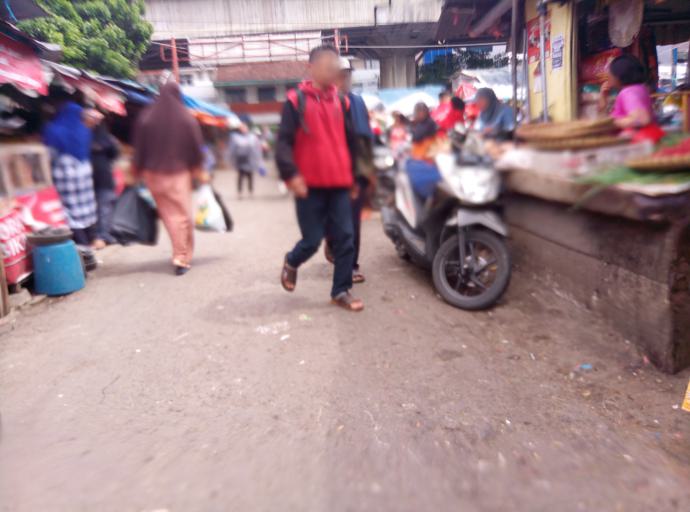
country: ID
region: West Java
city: Bandung
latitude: -6.9265
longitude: 107.6449
